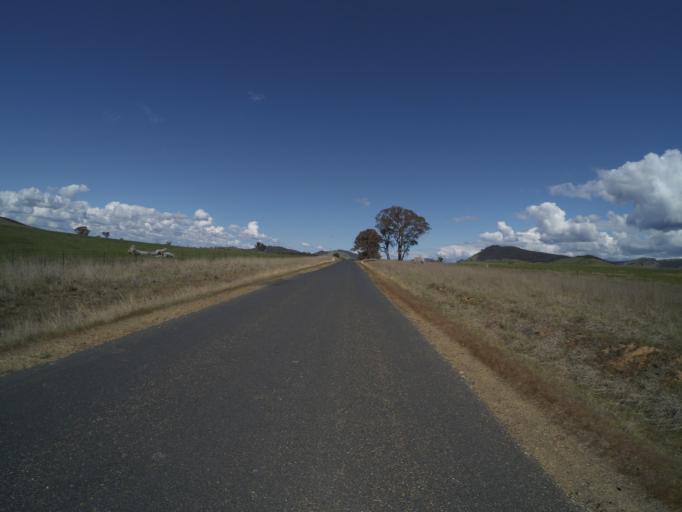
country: AU
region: New South Wales
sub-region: Yass Valley
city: Murrumbateman
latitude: -35.1222
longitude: 148.8674
